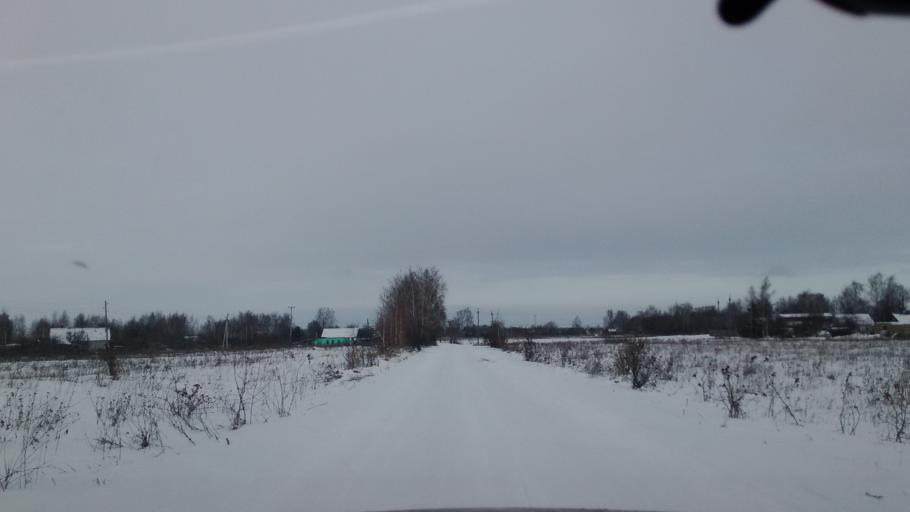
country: RU
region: Tula
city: Bogoroditsk
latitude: 53.7488
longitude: 38.1067
